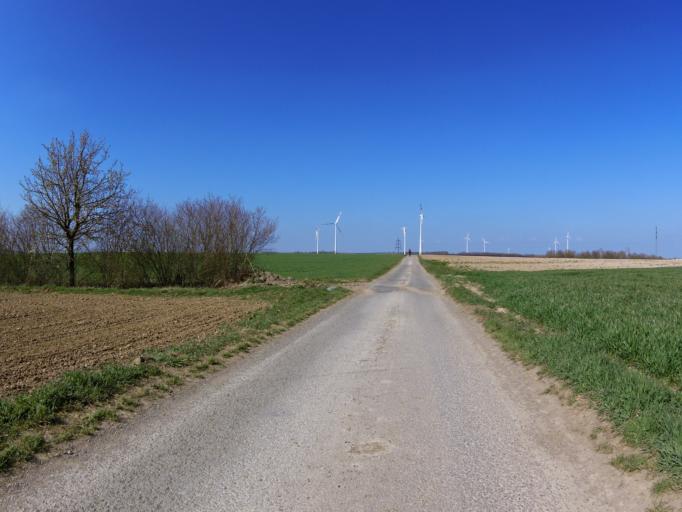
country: DE
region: Bavaria
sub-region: Regierungsbezirk Unterfranken
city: Biebelried
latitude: 49.7401
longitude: 10.1013
